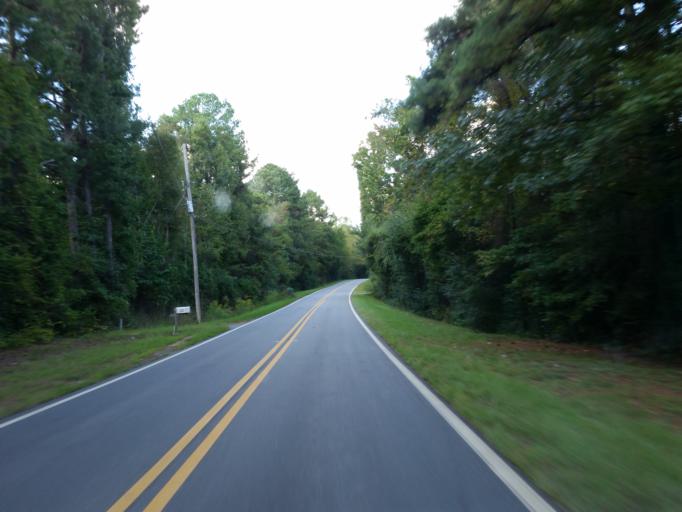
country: US
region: Georgia
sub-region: Butts County
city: Indian Springs
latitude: 33.1985
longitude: -84.0044
